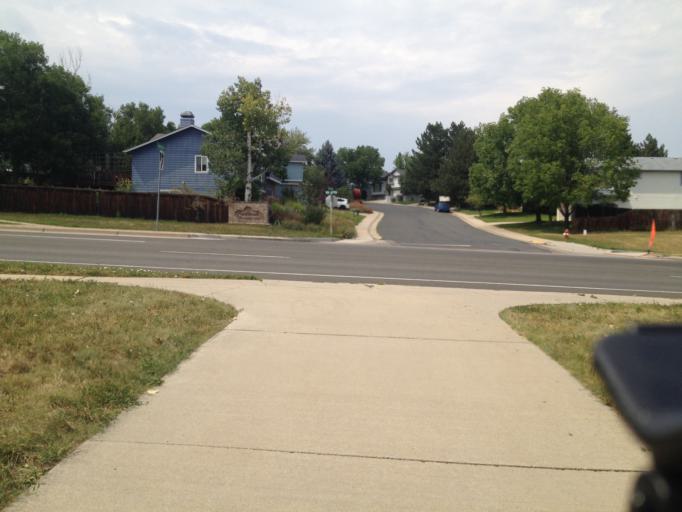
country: US
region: Colorado
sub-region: Boulder County
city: Louisville
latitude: 39.9797
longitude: -105.1468
